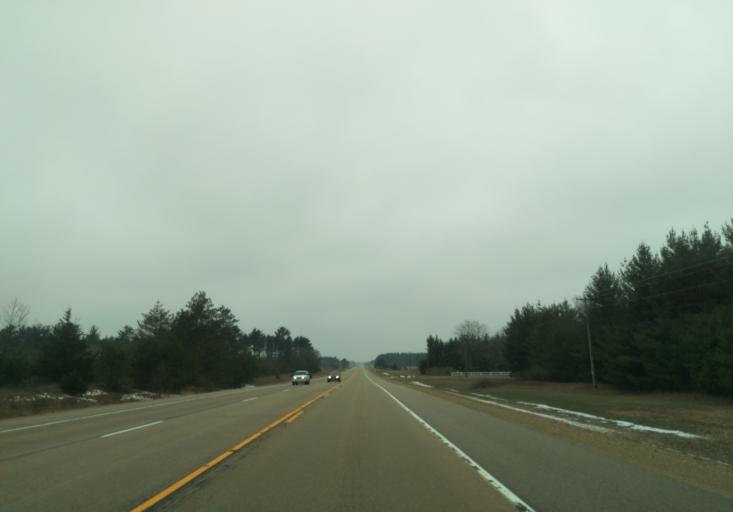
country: US
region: Wisconsin
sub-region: Sauk County
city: Spring Green
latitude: 43.1616
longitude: -89.9851
